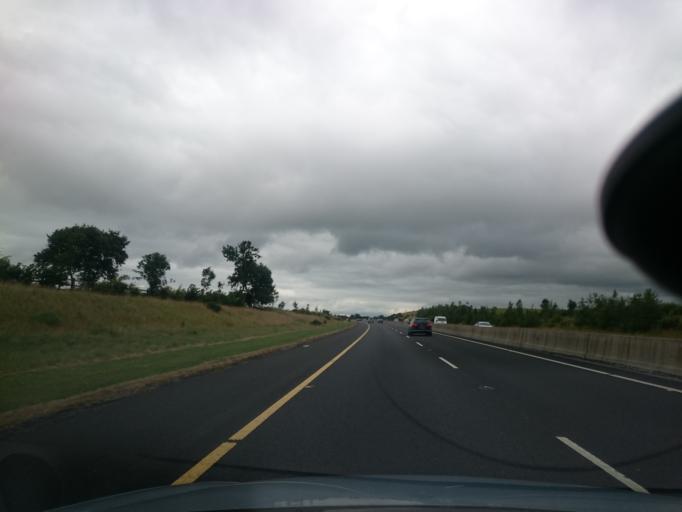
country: IE
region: Leinster
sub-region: Kildare
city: Old Kilcullen
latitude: 53.0684
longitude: -6.7615
